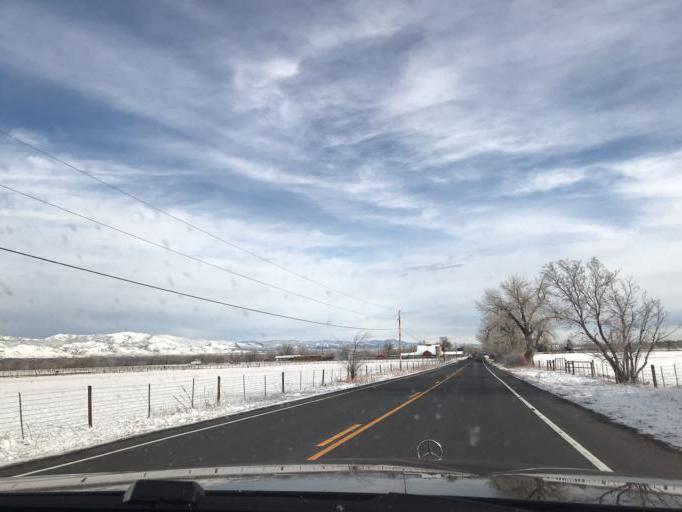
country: US
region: Colorado
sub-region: Boulder County
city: Superior
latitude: 39.9810
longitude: -105.2128
